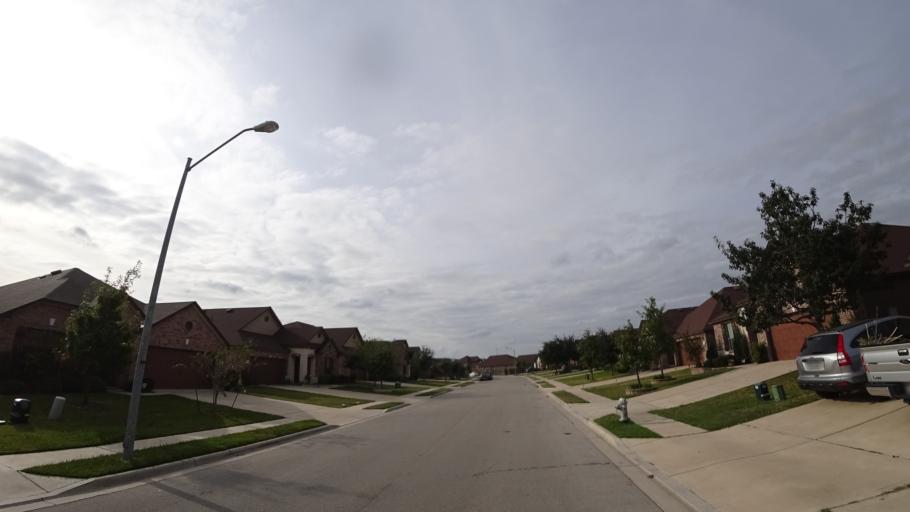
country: US
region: Texas
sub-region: Travis County
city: Wells Branch
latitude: 30.4303
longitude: -97.6612
